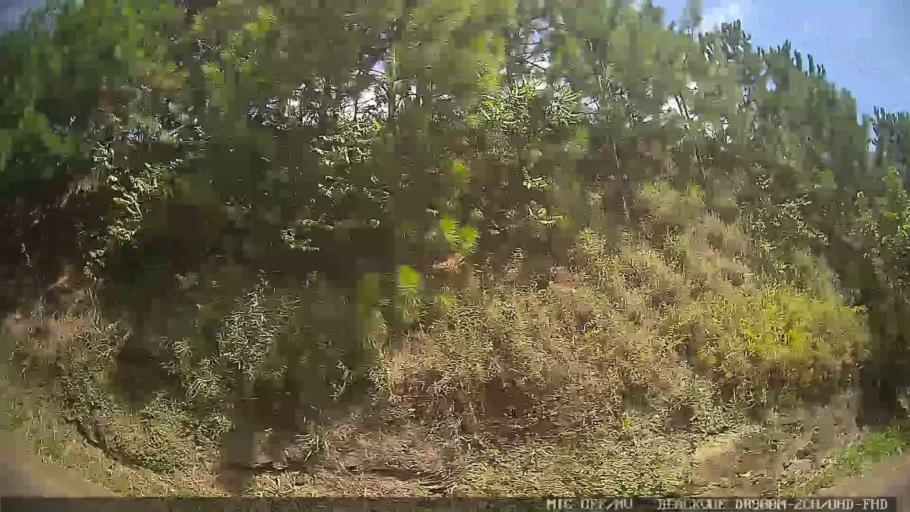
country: BR
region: Sao Paulo
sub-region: Tiete
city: Tiete
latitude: -23.1168
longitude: -47.7293
